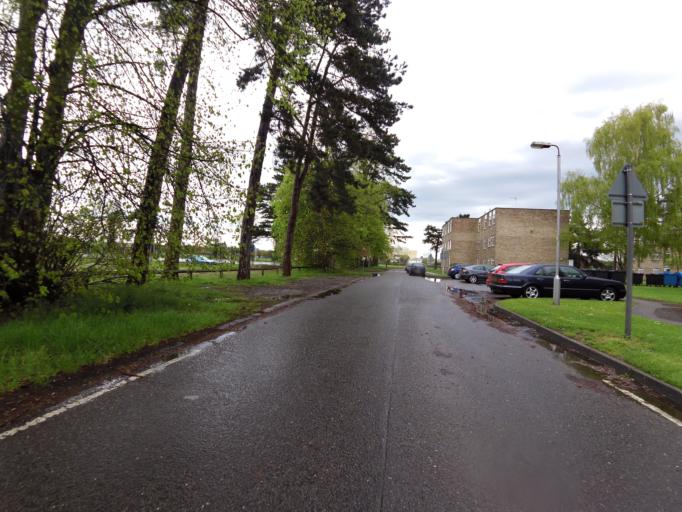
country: GB
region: England
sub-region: Suffolk
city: Kesgrave
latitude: 52.0525
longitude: 1.1986
